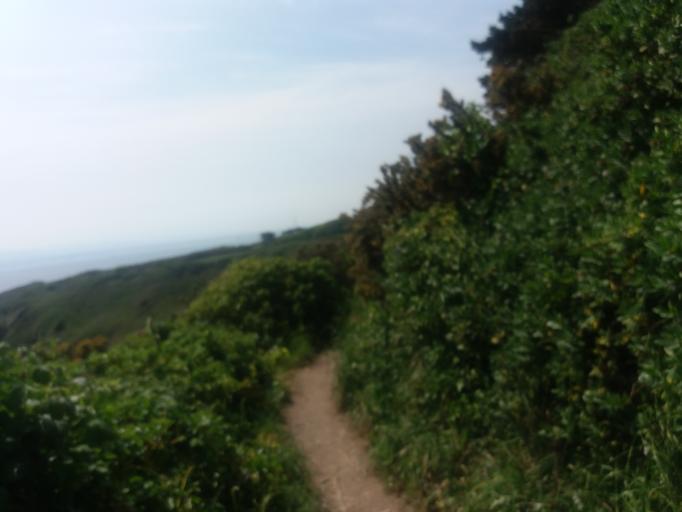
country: IE
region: Leinster
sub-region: Fingal County
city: Howth
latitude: 53.3625
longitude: -6.0731
